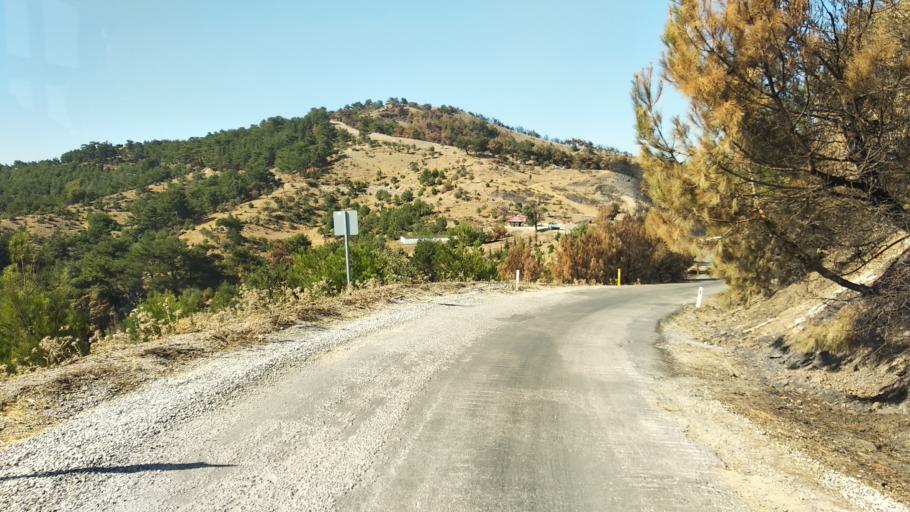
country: TR
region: Izmir
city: Gaziemir
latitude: 38.2919
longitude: 27.0009
